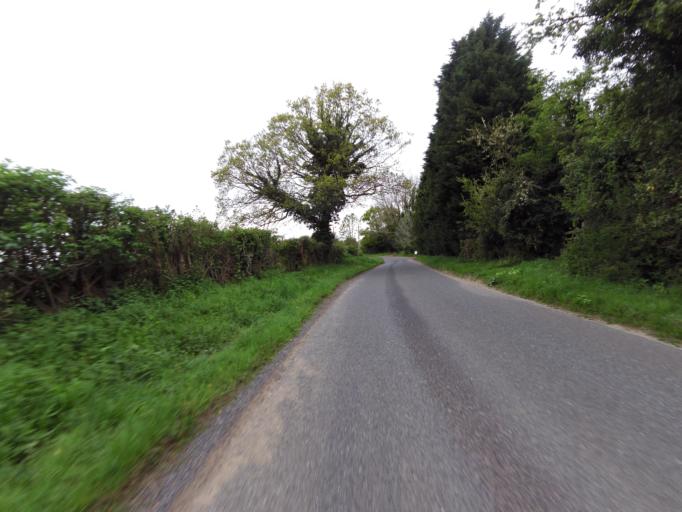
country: GB
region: England
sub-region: Suffolk
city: Kesgrave
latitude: 52.0092
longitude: 1.2426
